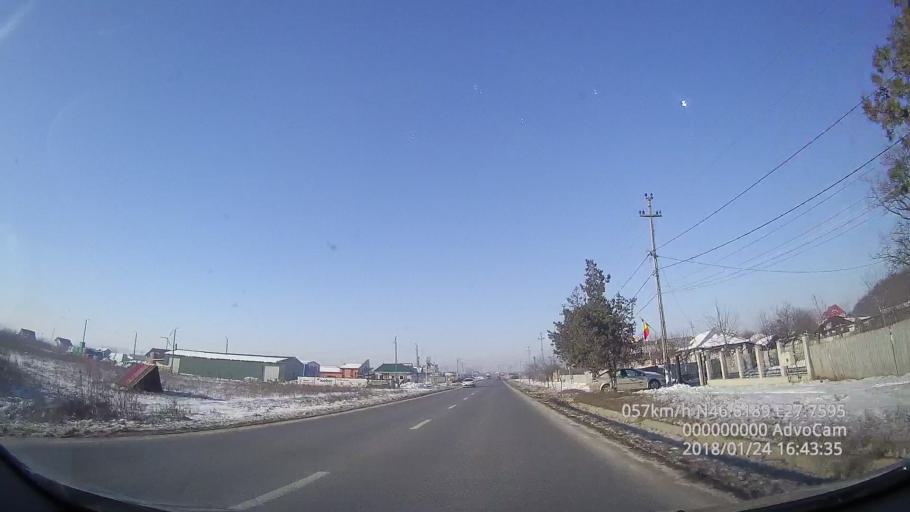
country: RO
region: Vaslui
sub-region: Comuna Muntenii de Jos
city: Muntenii de Jos
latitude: 46.6192
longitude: 27.7592
